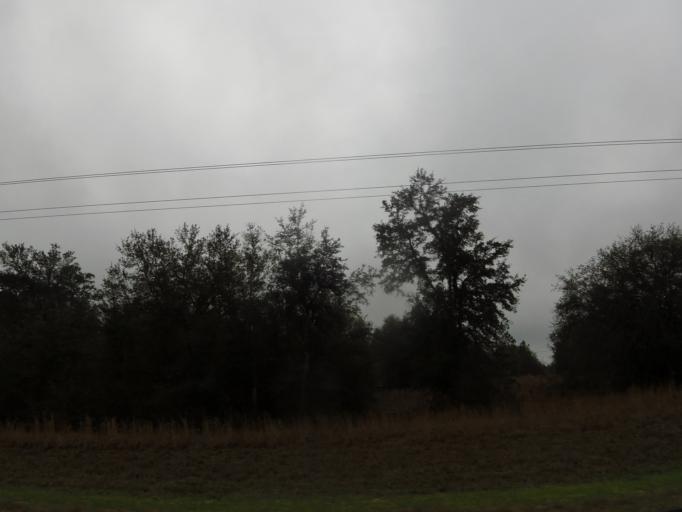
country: US
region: Florida
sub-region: Gilchrist County
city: Trenton
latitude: 29.7961
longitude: -82.8498
